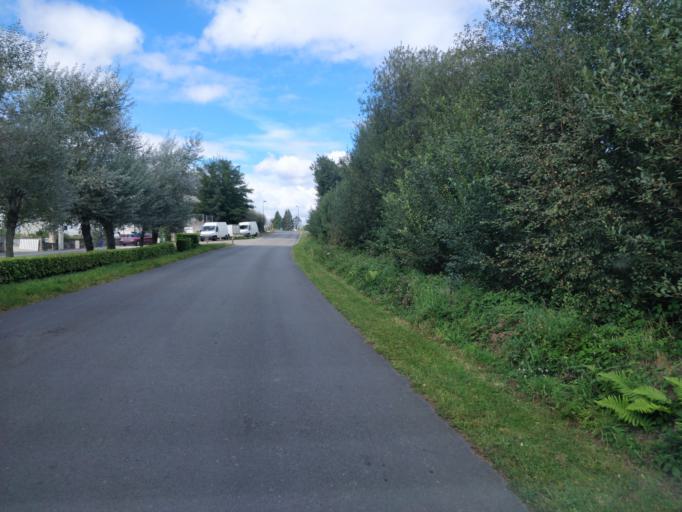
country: FR
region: Brittany
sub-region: Departement du Finistere
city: Lampaul-Guimiliau
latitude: 48.4911
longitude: -4.0345
